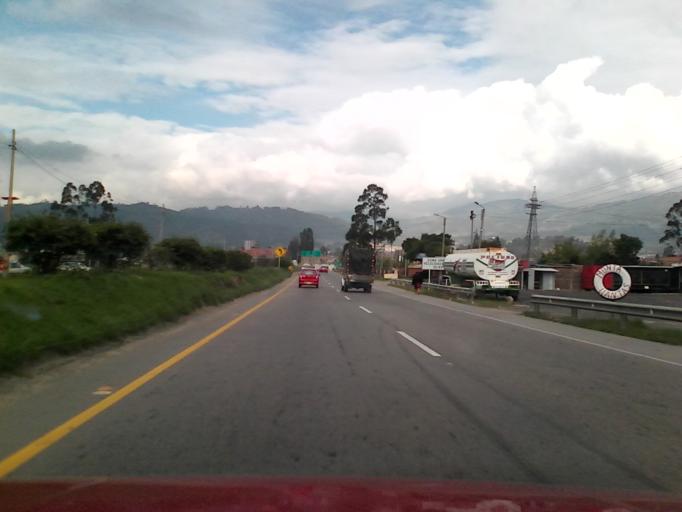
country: CO
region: Boyaca
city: Duitama
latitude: 5.8087
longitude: -73.0119
